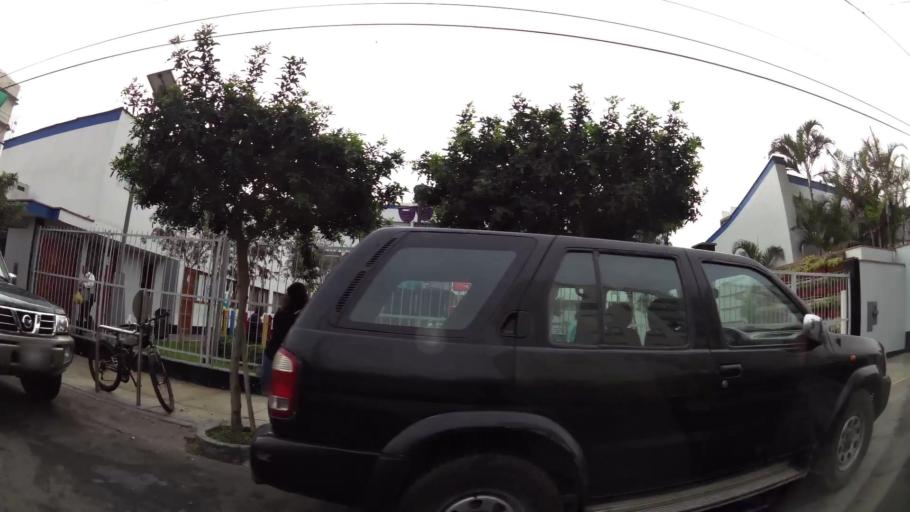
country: PE
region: Lima
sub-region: Lima
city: San Isidro
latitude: -12.1112
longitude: -77.0494
